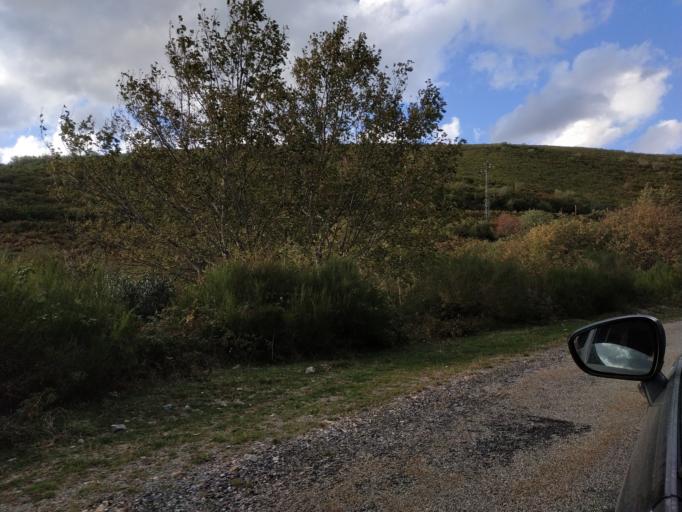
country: ES
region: Castille and Leon
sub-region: Provincia de Leon
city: Candin
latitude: 42.8703
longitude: -6.8353
